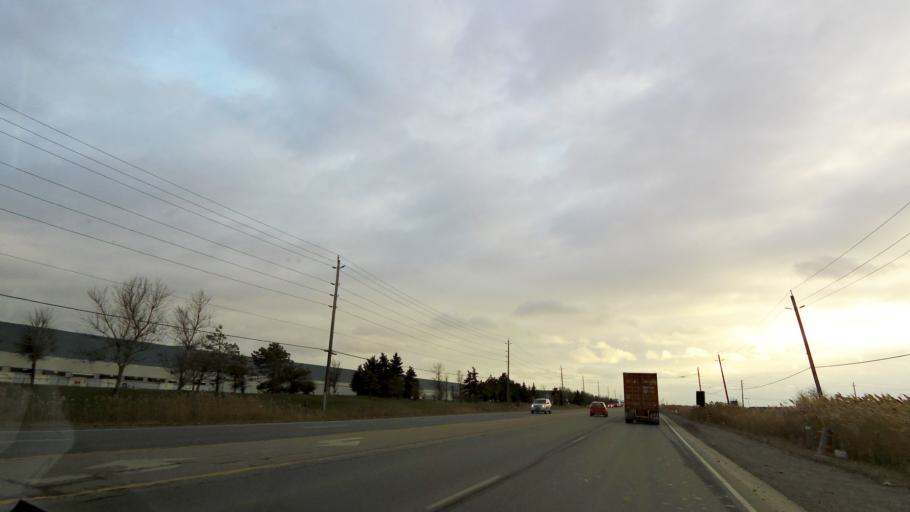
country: CA
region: Ontario
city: Brampton
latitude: 43.8092
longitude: -79.6728
